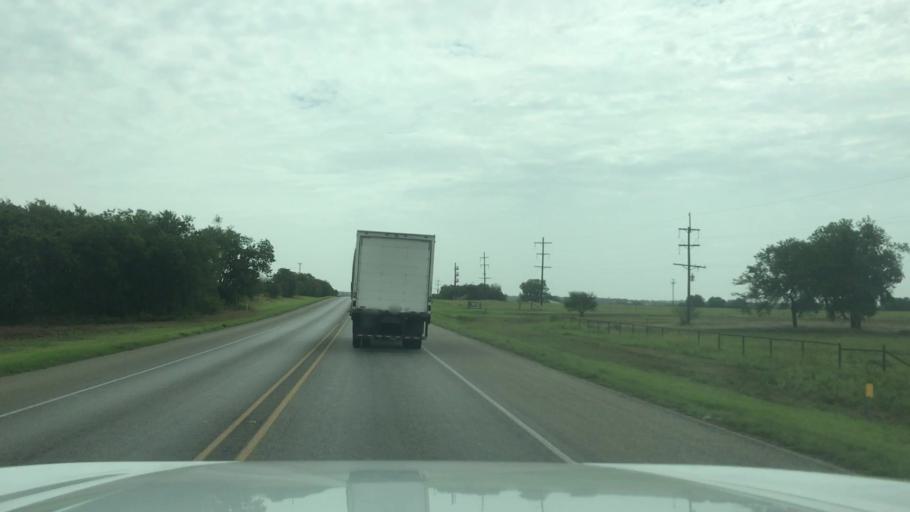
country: US
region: Texas
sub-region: Comanche County
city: De Leon
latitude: 32.0976
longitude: -98.4642
